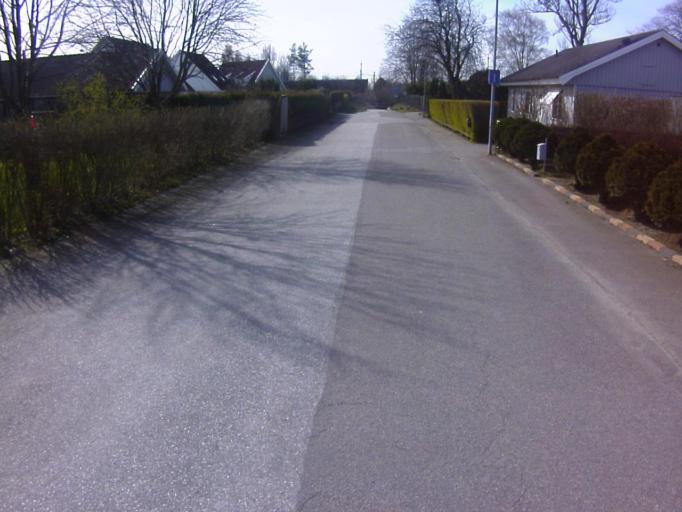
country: SE
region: Skane
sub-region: Kavlinge Kommun
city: Kaevlinge
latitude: 55.8070
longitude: 13.1123
